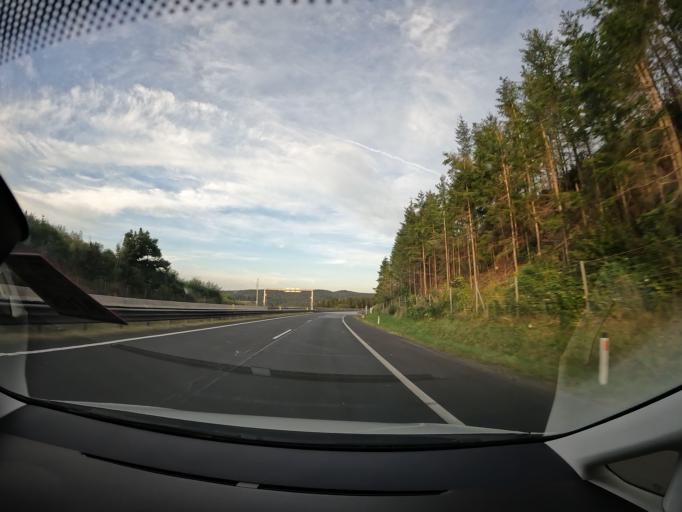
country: AT
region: Styria
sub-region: Politischer Bezirk Voitsberg
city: Modriach
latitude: 46.9549
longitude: 15.0205
